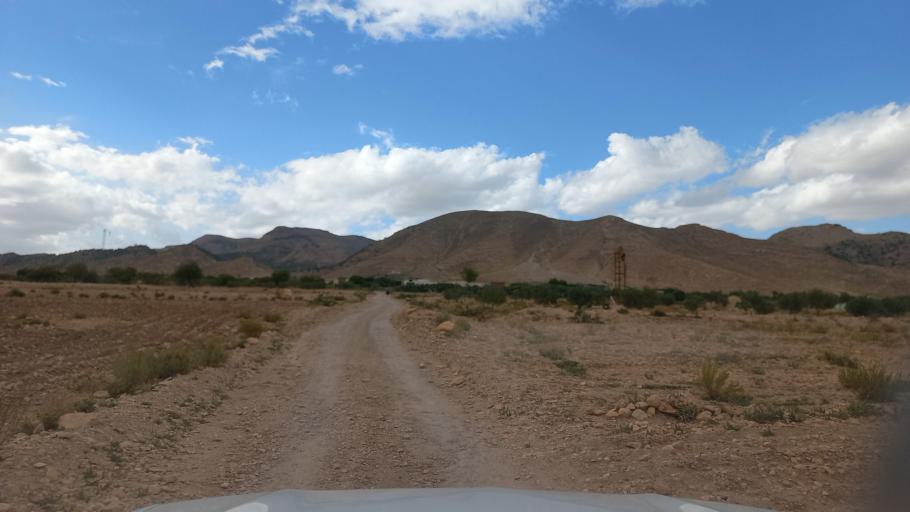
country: TN
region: Al Qasrayn
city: Sbiba
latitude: 35.4484
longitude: 9.0730
